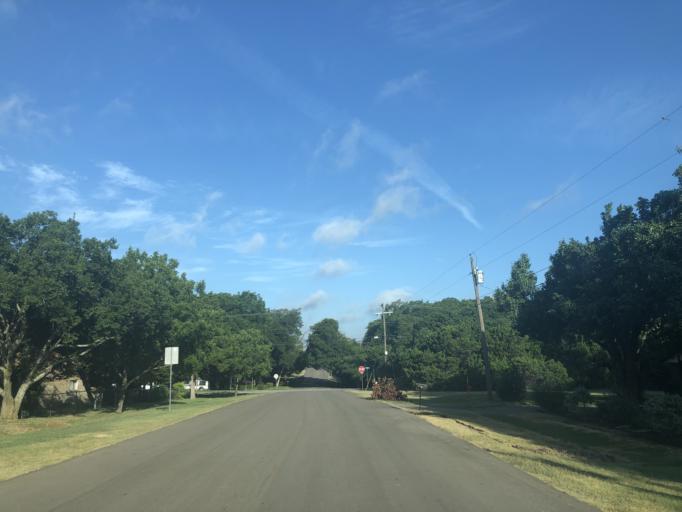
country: US
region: Texas
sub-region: Dallas County
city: Duncanville
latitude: 32.6684
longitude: -96.9145
